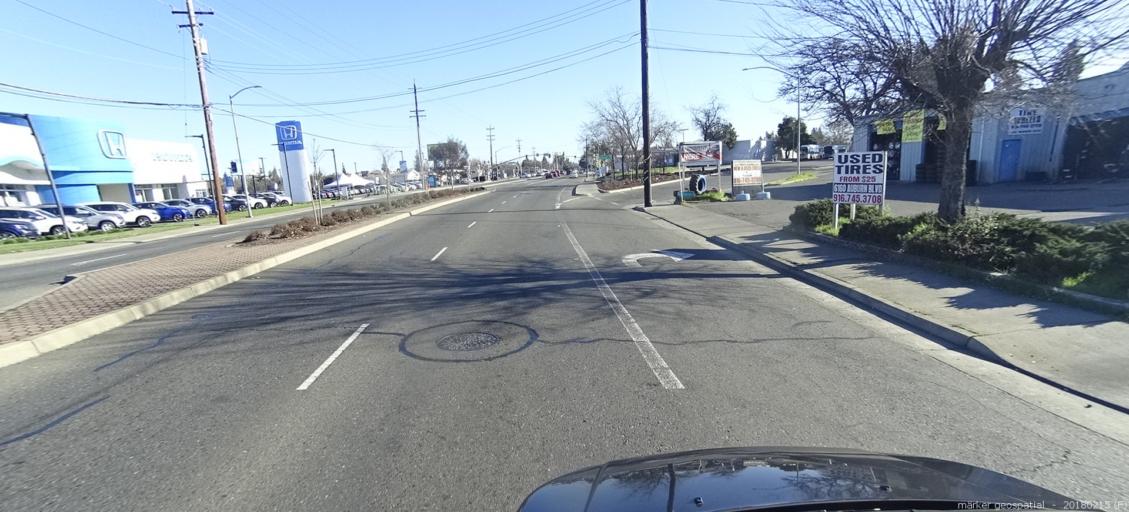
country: US
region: California
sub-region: Sacramento County
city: Foothill Farms
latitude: 38.6778
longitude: -121.3225
